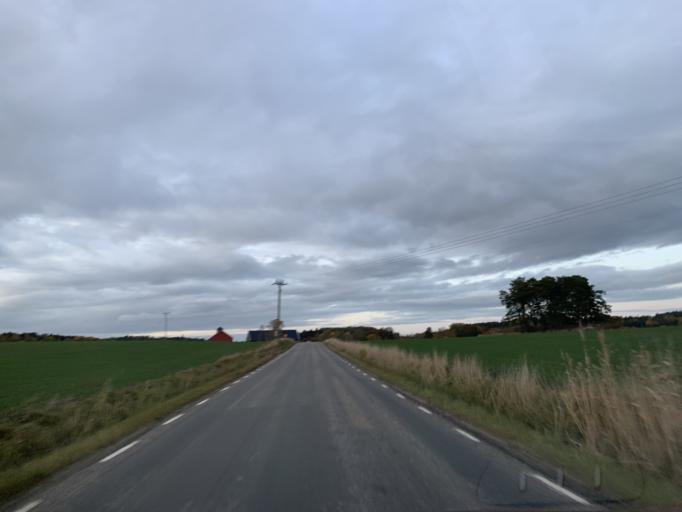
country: SE
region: Stockholm
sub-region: Nynashamns Kommun
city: Osmo
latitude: 58.9530
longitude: 17.7668
